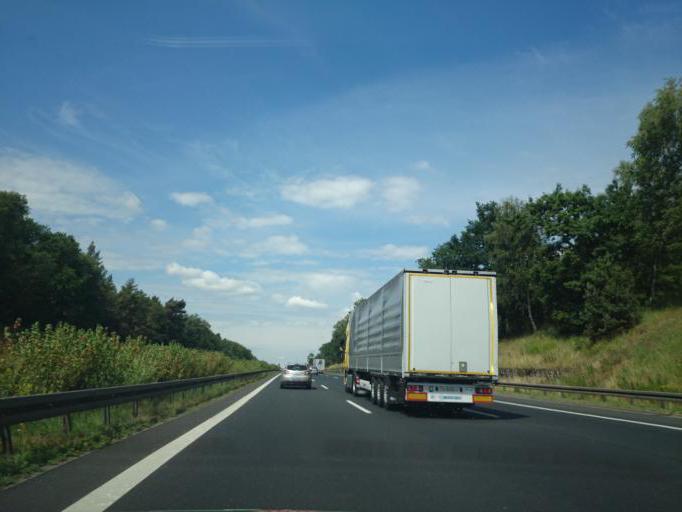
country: DE
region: Brandenburg
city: Rangsdorf
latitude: 52.3060
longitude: 13.4134
